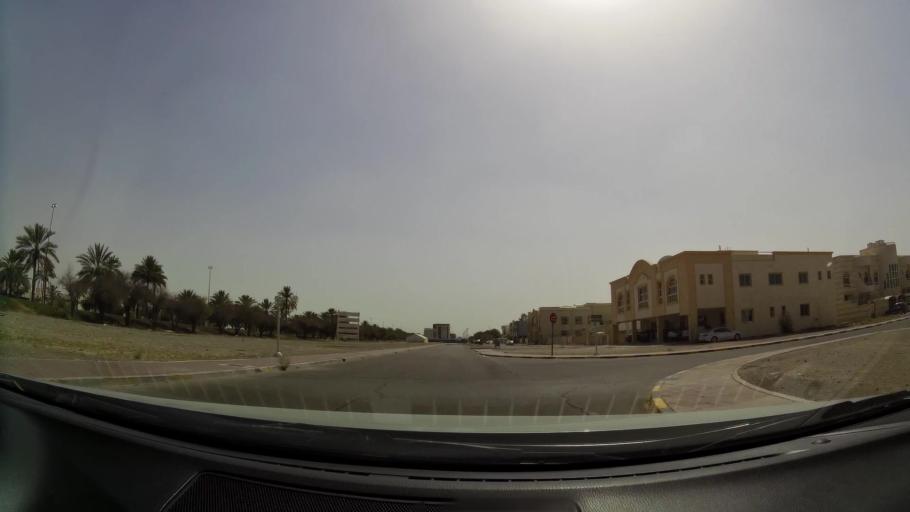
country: AE
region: Abu Dhabi
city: Al Ain
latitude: 24.2206
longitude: 55.6914
